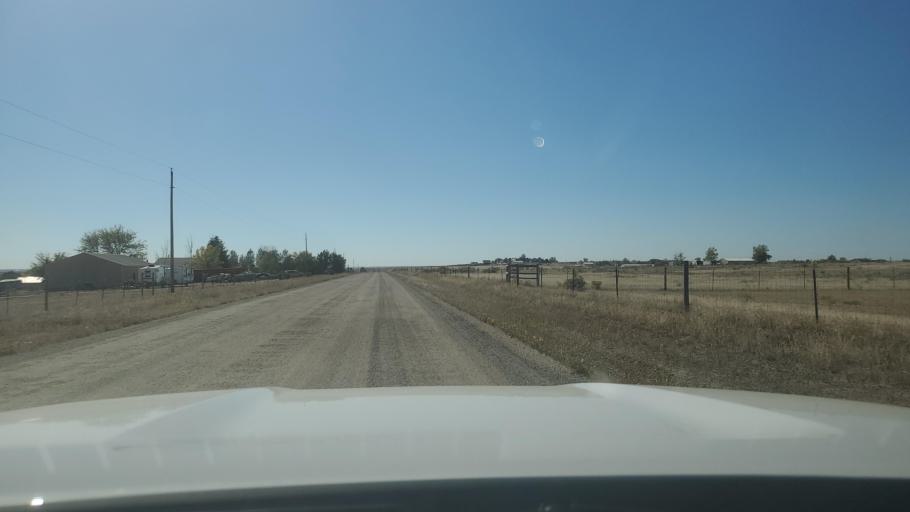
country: US
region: Colorado
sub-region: Adams County
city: Bennett
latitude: 39.7739
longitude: -104.3769
